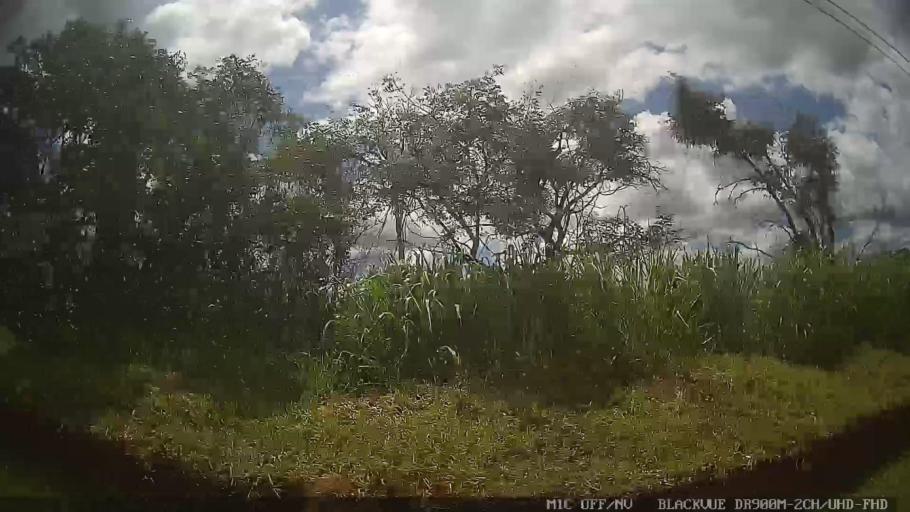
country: BR
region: Sao Paulo
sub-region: Atibaia
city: Atibaia
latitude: -23.0674
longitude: -46.5119
